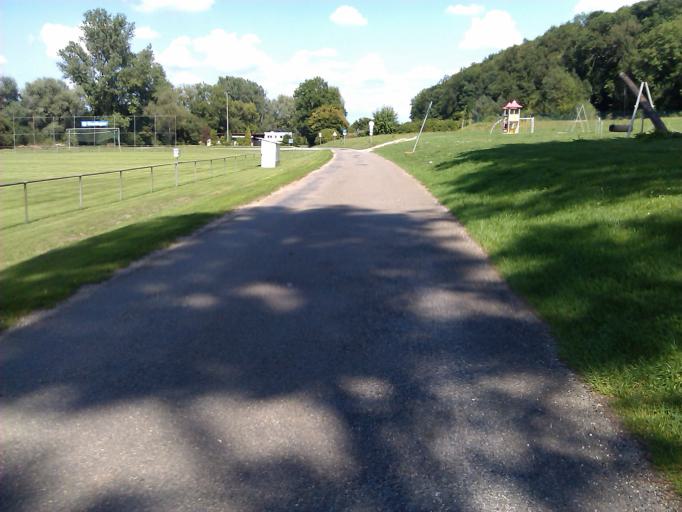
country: DE
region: Baden-Wuerttemberg
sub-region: Regierungsbezirk Stuttgart
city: Neckartenzlingen
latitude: 48.5957
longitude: 9.2472
